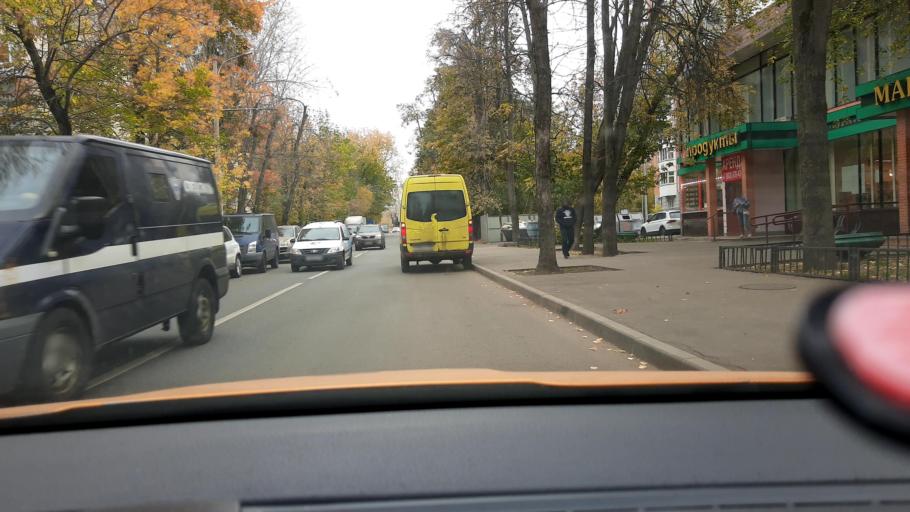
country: RU
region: Moscow
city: Leonovo
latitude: 55.8594
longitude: 37.6442
